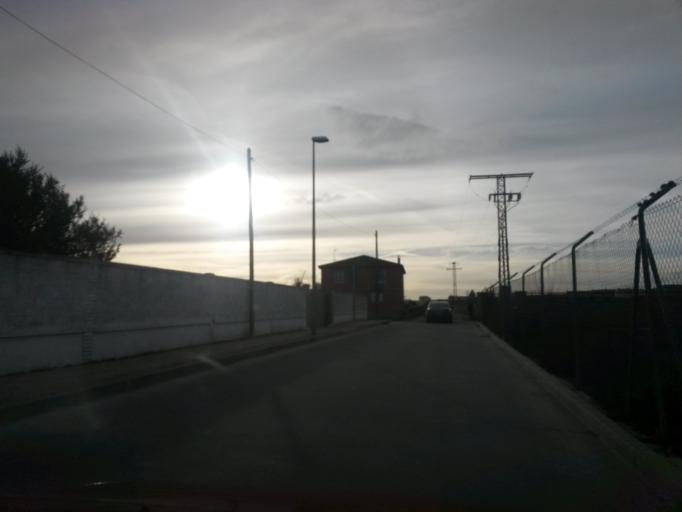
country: ES
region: Castille and Leon
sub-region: Provincia de Salamanca
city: Santa Marta de Tormes
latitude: 40.9668
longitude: -5.6285
